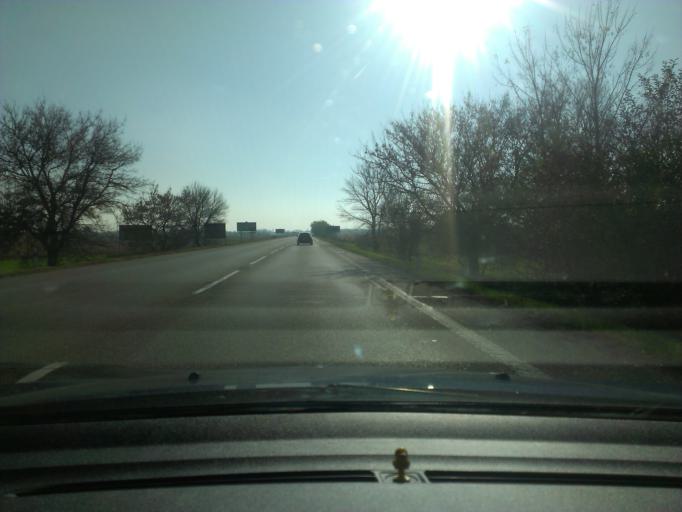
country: SK
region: Nitriansky
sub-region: Okres Nove Zamky
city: Nove Zamky
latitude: 47.9526
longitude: 18.1929
